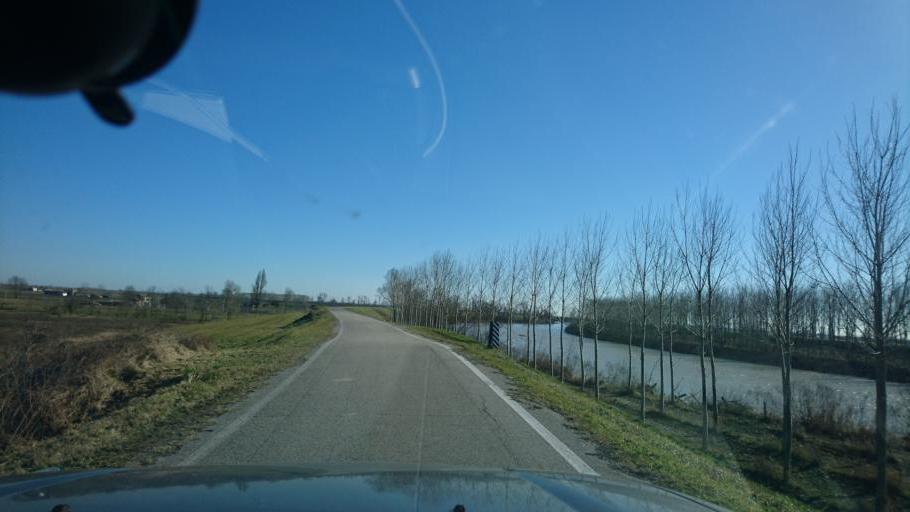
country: IT
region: Veneto
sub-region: Provincia di Rovigo
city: Ariano
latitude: 44.9334
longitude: 12.1333
